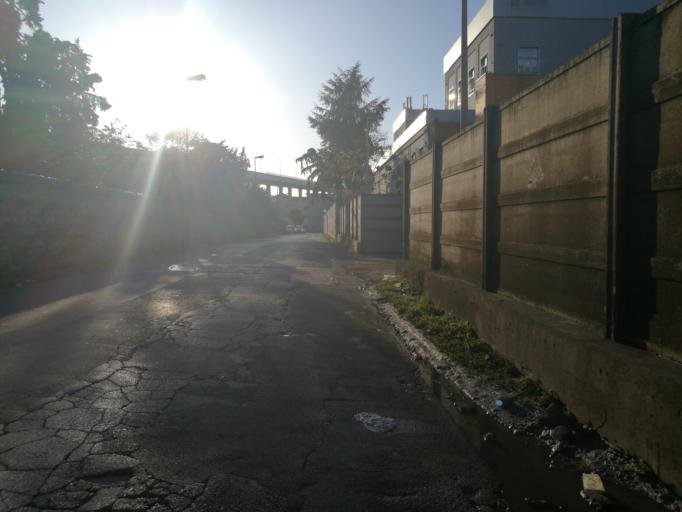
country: IT
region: Campania
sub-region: Provincia di Napoli
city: Casavatore
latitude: 40.8647
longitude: 14.2836
